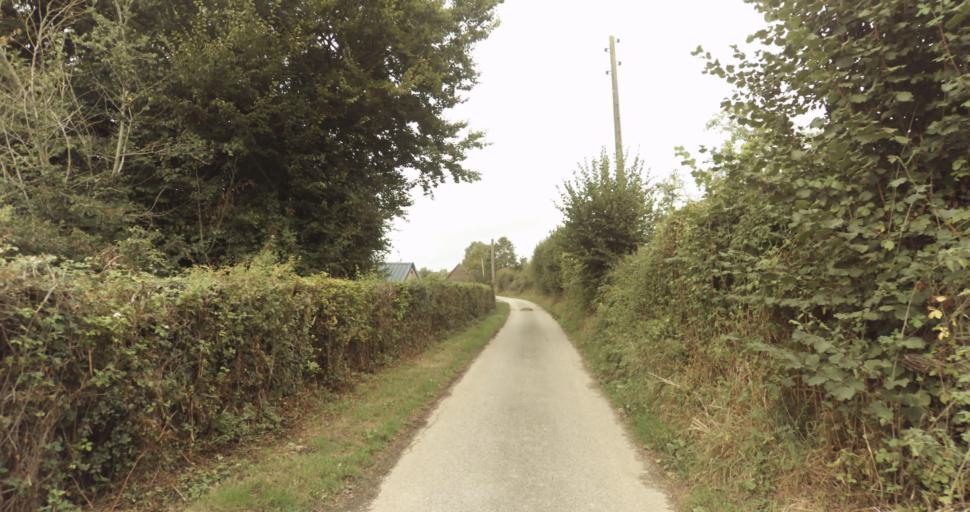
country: FR
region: Lower Normandy
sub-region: Departement de l'Orne
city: Gace
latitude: 48.8204
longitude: 0.2853
